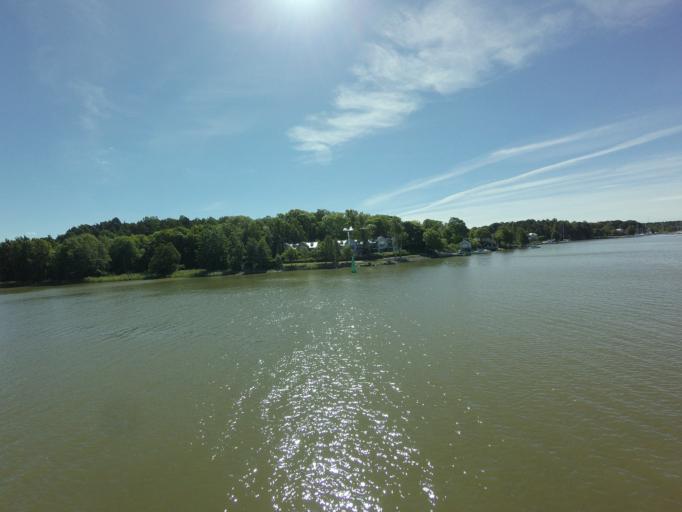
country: FI
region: Varsinais-Suomi
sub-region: Turku
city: Raisio
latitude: 60.4304
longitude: 22.1980
